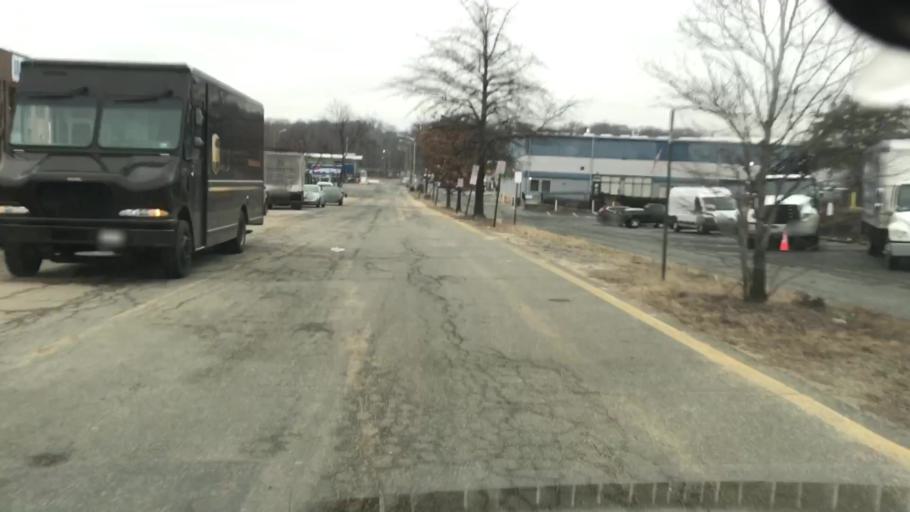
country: US
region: Virginia
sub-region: Fairfax County
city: Newington
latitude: 38.7278
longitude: -77.1962
